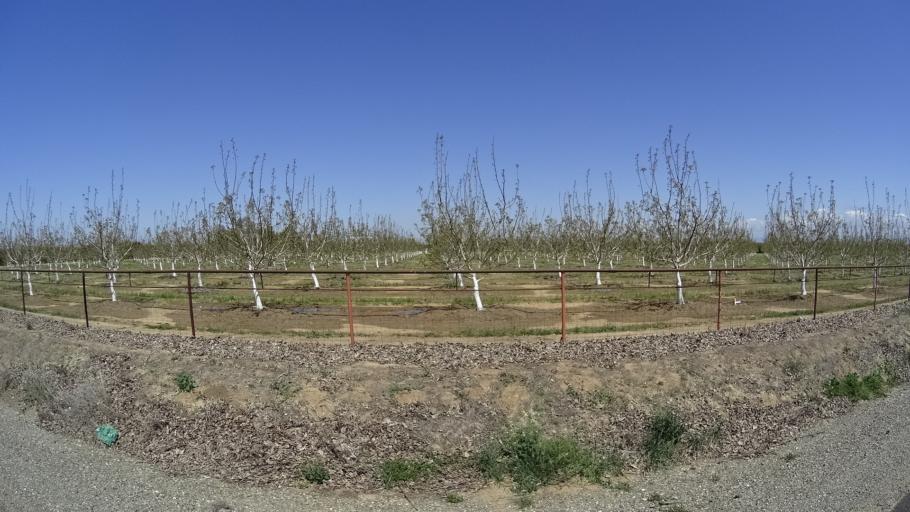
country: US
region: California
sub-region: Glenn County
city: Hamilton City
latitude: 39.7665
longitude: -122.0417
